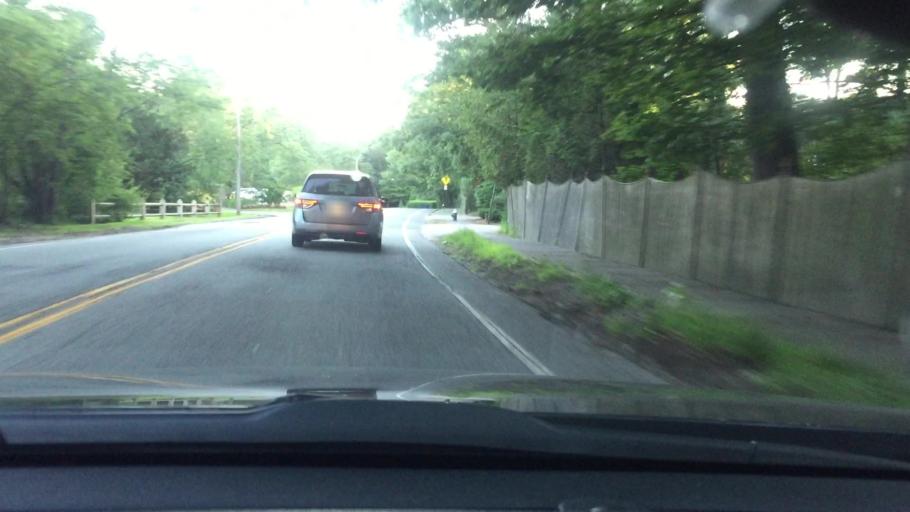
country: US
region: Massachusetts
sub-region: Suffolk County
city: Jamaica Plain
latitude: 42.3142
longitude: -71.1378
